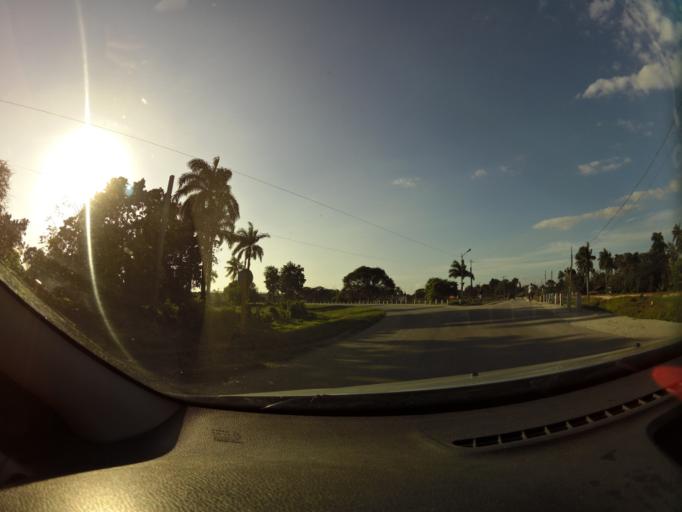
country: CU
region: Granma
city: Jiguani
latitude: 20.3627
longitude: -76.4232
